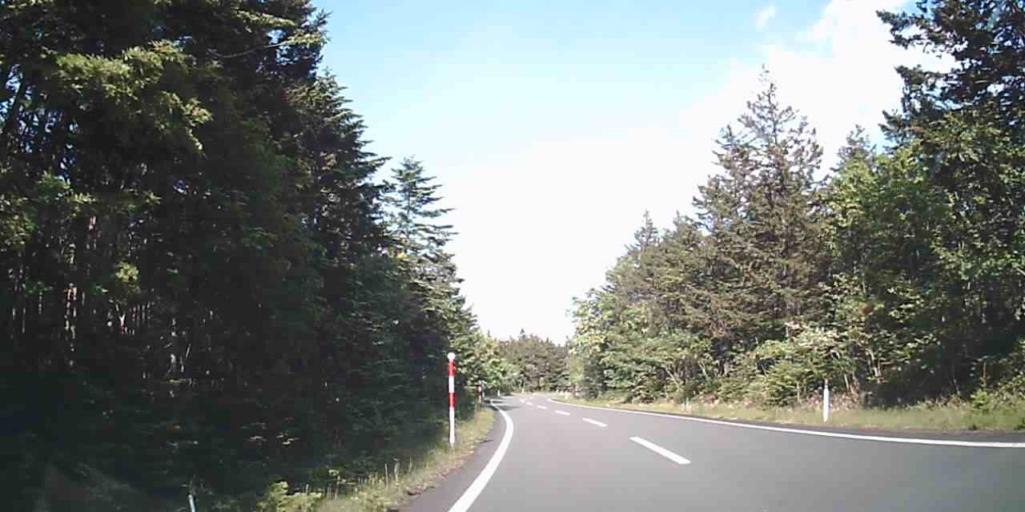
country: JP
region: Hokkaido
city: Shiraoi
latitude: 42.6885
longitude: 141.4319
